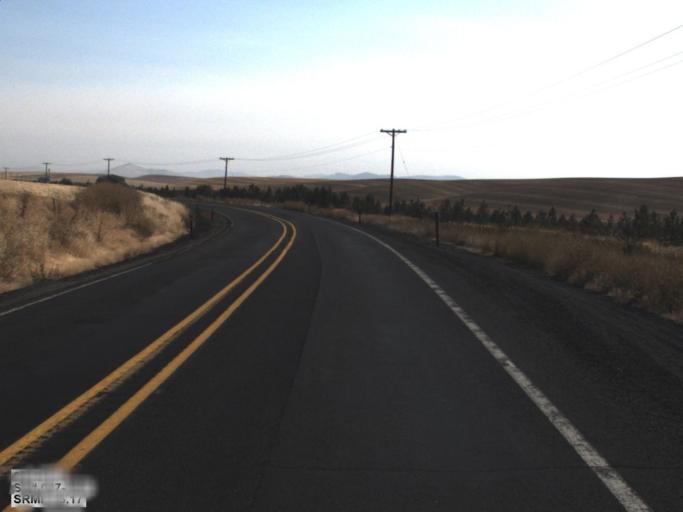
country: US
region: Washington
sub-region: Whitman County
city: Colfax
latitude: 47.1208
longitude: -117.2209
